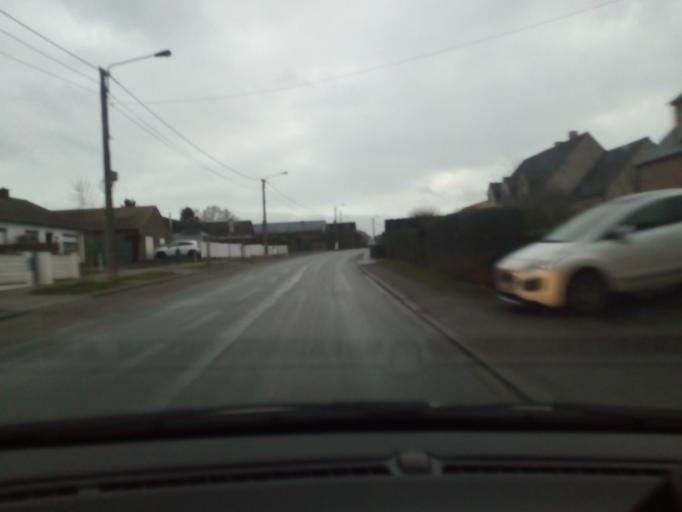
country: BE
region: Wallonia
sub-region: Province du Hainaut
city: Estinnes-au-Val
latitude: 50.4438
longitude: 4.0995
